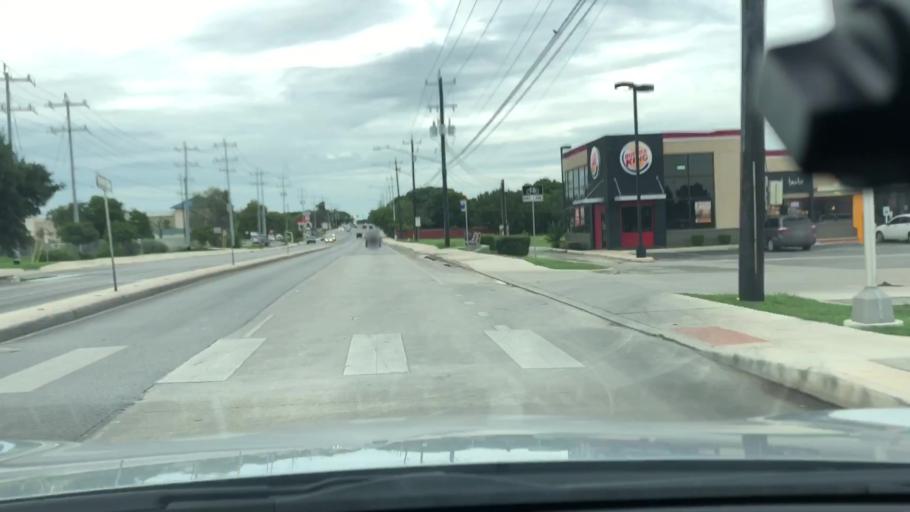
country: US
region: Texas
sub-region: Bexar County
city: Leon Valley
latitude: 29.4867
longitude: -98.6657
